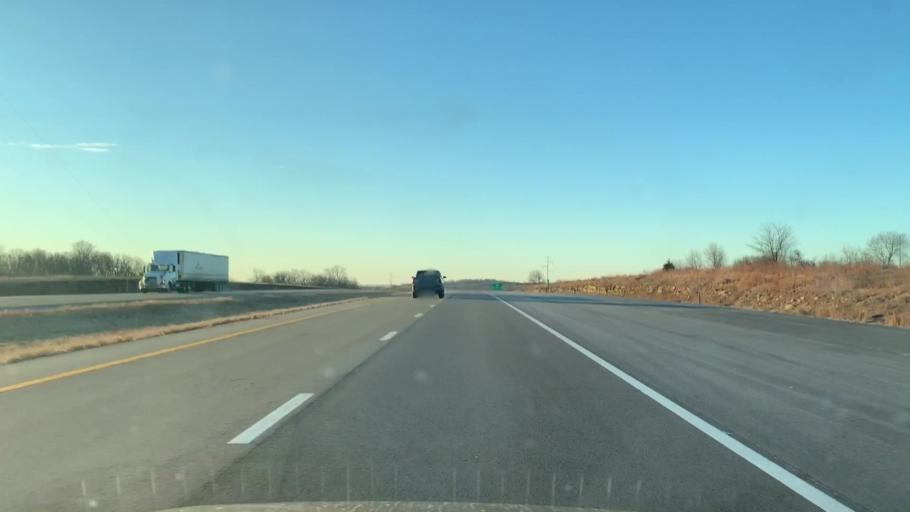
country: US
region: Kansas
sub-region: Linn County
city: La Cygne
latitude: 38.3679
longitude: -94.6877
